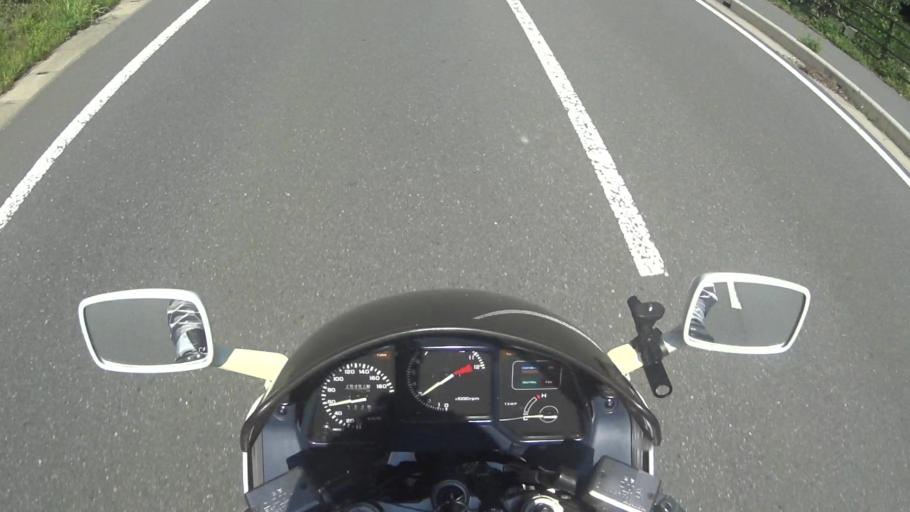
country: JP
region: Kyoto
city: Miyazu
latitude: 35.6832
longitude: 135.2888
